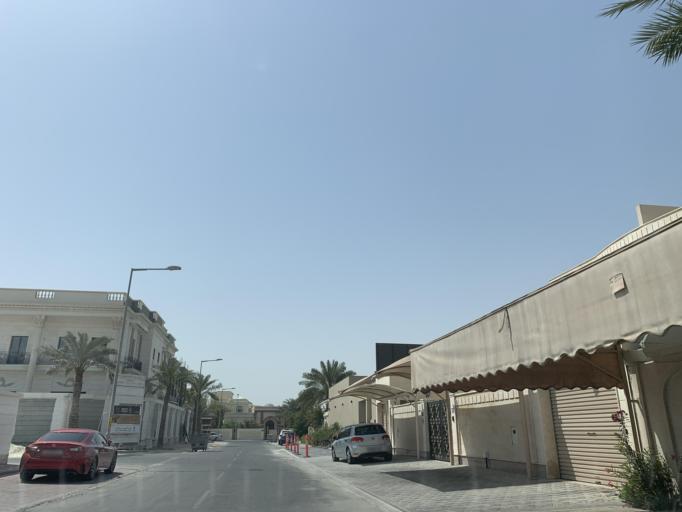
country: BH
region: Manama
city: Manama
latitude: 26.2019
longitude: 50.5691
